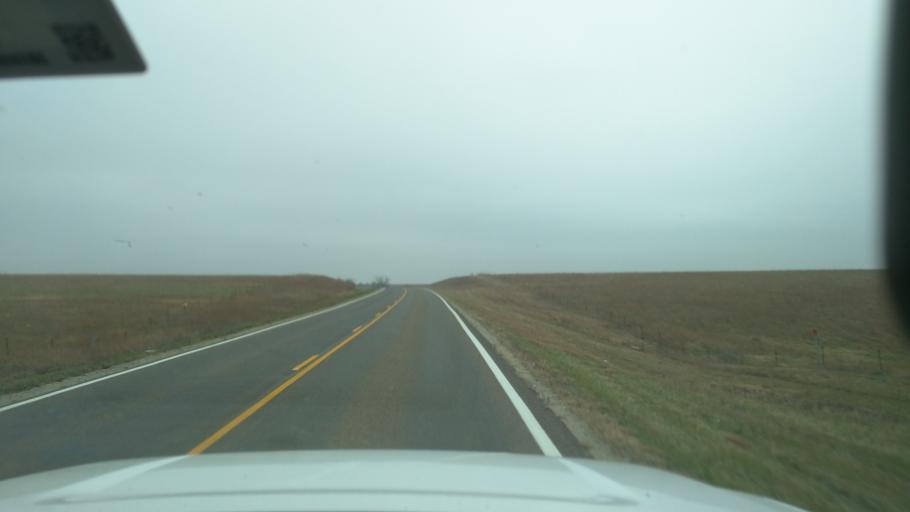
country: US
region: Kansas
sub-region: Morris County
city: Council Grove
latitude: 38.6594
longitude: -96.2693
